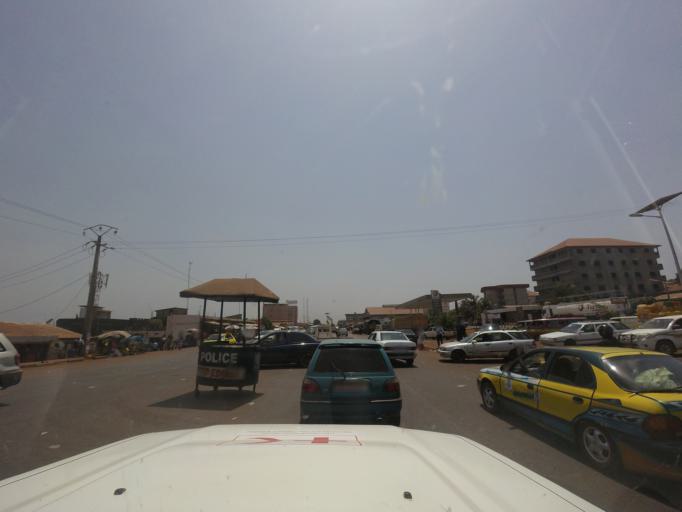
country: GN
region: Conakry
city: Conakry
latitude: 9.6340
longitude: -13.5717
